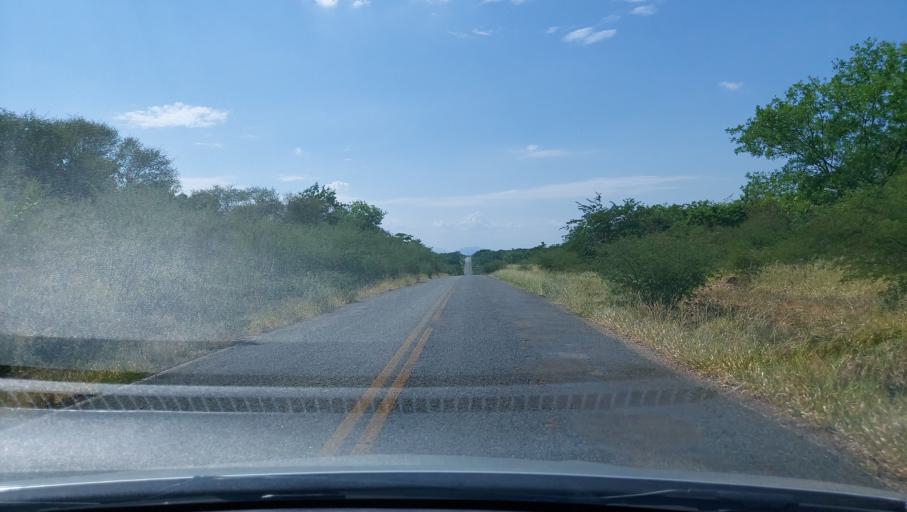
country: BR
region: Bahia
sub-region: Oliveira Dos Brejinhos
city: Beira Rio
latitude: -12.1701
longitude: -42.5459
